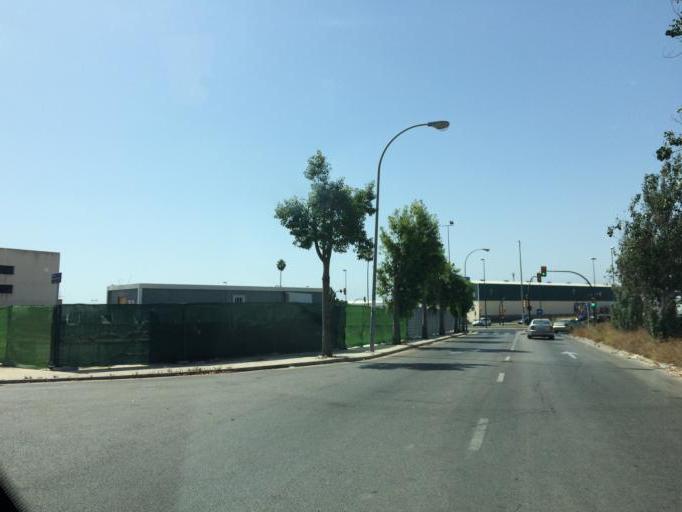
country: ES
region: Andalusia
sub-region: Provincia de Malaga
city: Malaga
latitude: 36.7077
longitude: -4.4716
